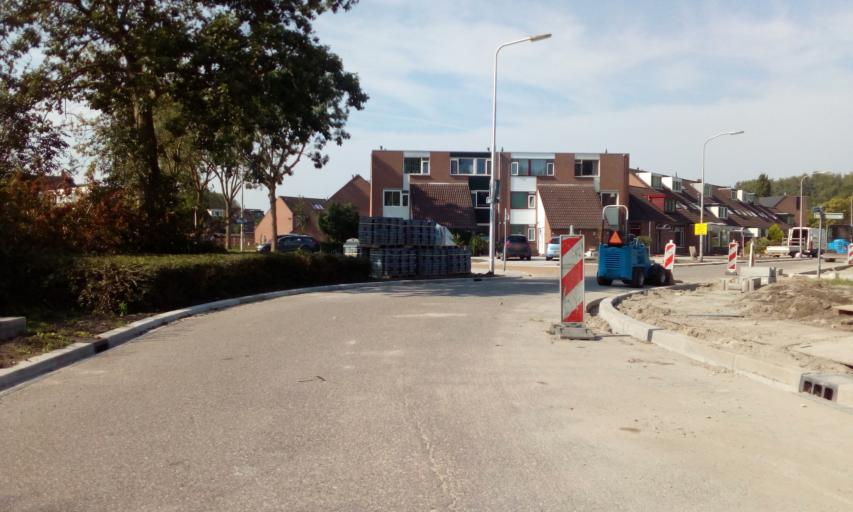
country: NL
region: South Holland
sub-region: Gemeente Krimpen aan den IJssel
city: Krimpen aan den IJssel
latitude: 51.9775
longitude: 4.6187
